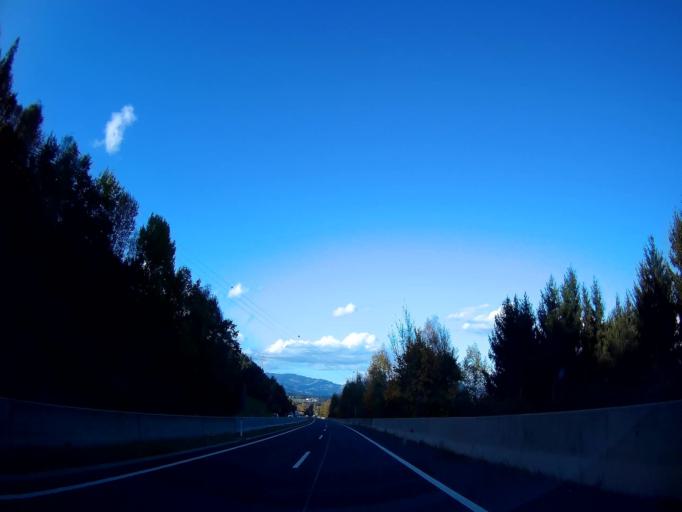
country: AT
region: Carinthia
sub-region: Politischer Bezirk Wolfsberg
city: Sankt Andrae
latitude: 46.7553
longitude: 14.8165
